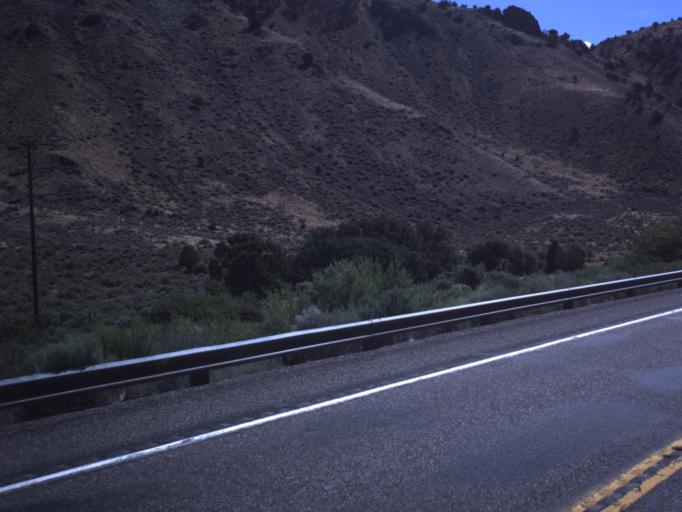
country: US
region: Utah
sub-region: Sevier County
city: Monroe
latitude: 38.4956
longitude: -112.2520
